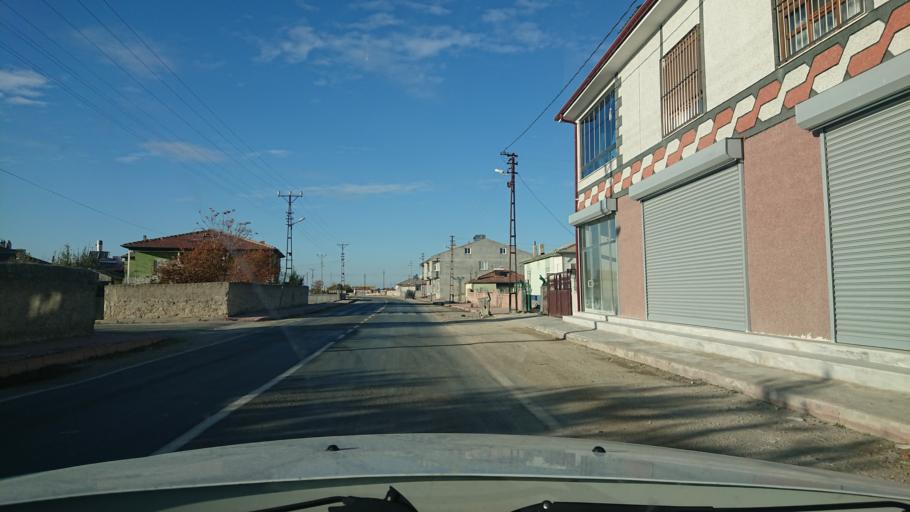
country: TR
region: Aksaray
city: Eskil
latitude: 38.5637
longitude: 33.1946
